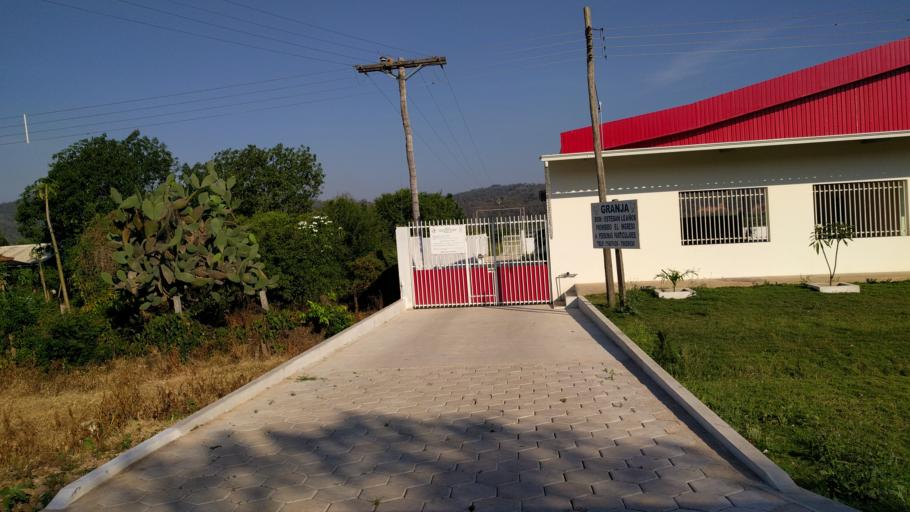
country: BO
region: Santa Cruz
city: Jorochito
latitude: -18.1322
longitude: -63.4710
